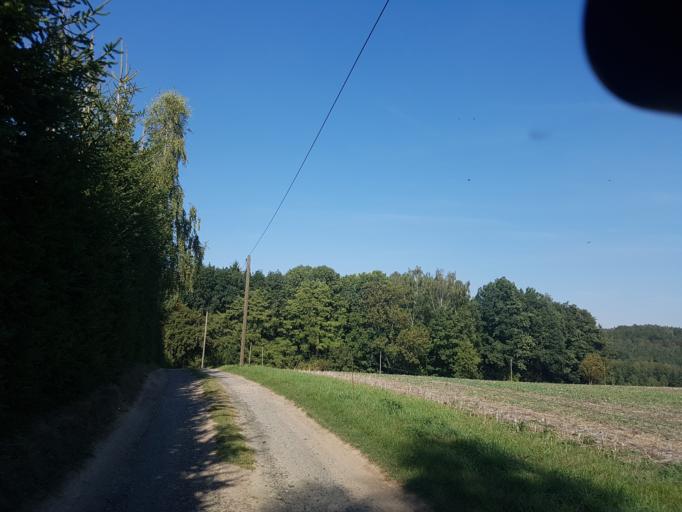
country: DE
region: Saxony
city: Kriebstein
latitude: 51.0460
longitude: 13.0070
